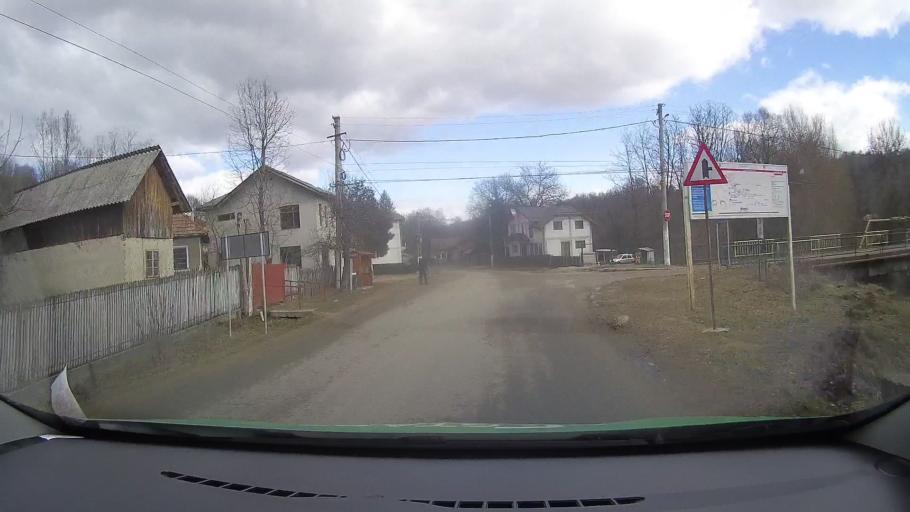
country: RO
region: Dambovita
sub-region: Comuna Buciumeni
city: Buciumeni
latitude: 45.1278
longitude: 25.4667
